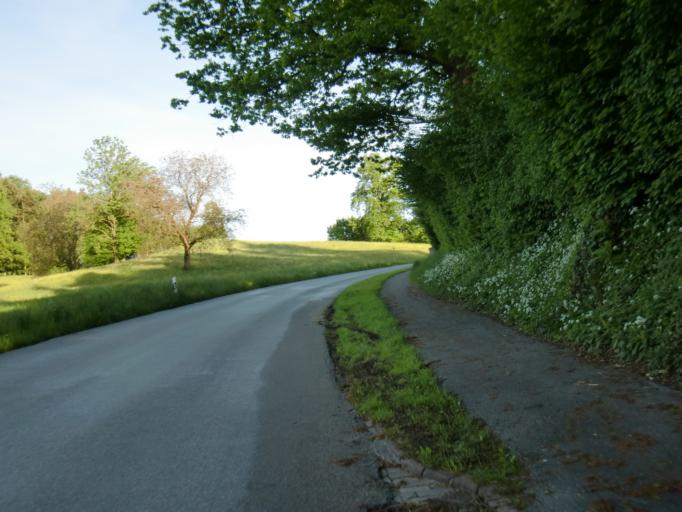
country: CH
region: Zurich
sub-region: Bezirk Hinwil
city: Binzikon
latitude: 47.2756
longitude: 8.7698
